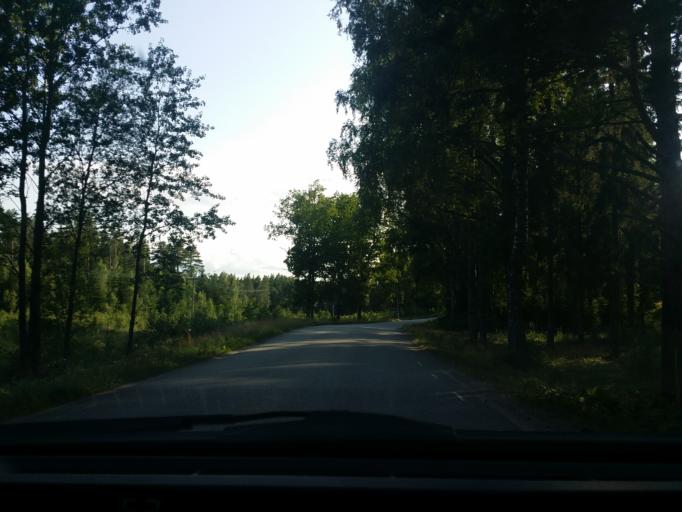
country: SE
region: Vaestmanland
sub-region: Vasteras
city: Tillberga
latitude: 59.5733
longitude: 16.6697
